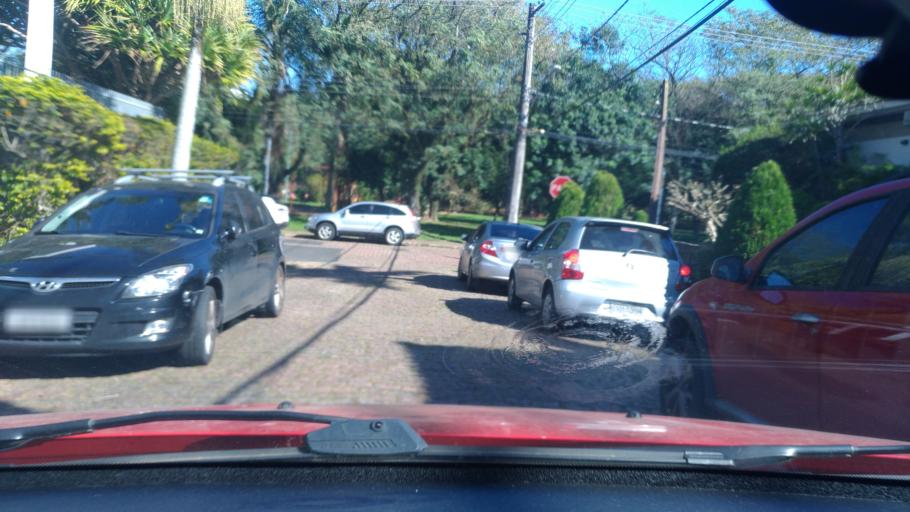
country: BR
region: Rio Grande do Sul
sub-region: Porto Alegre
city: Porto Alegre
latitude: -30.0303
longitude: -51.1684
